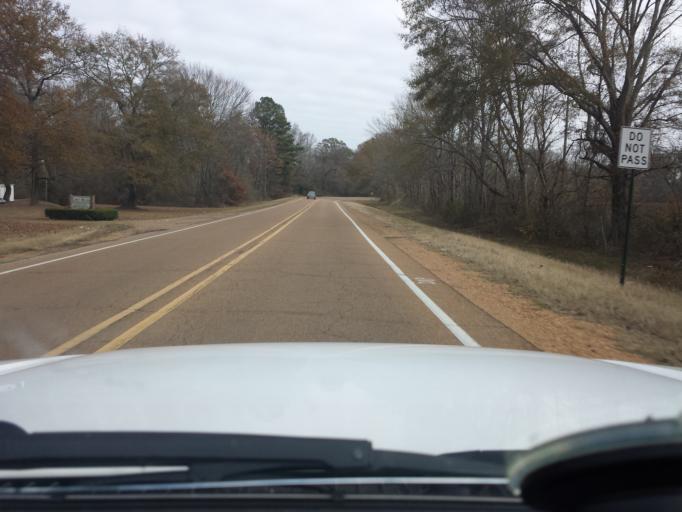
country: US
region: Mississippi
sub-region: Yazoo County
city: Yazoo City
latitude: 32.7977
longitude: -90.2171
